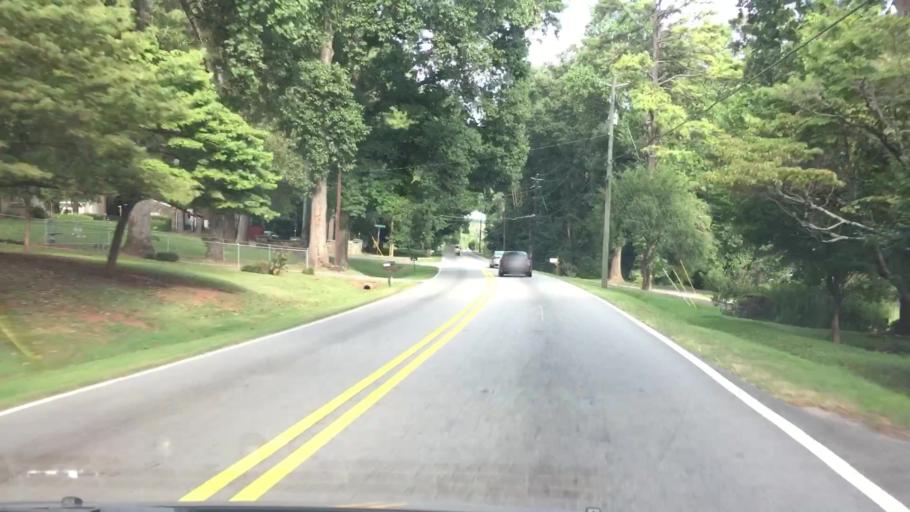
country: US
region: Georgia
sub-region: Clayton County
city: Conley
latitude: 33.6599
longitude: -84.2958
